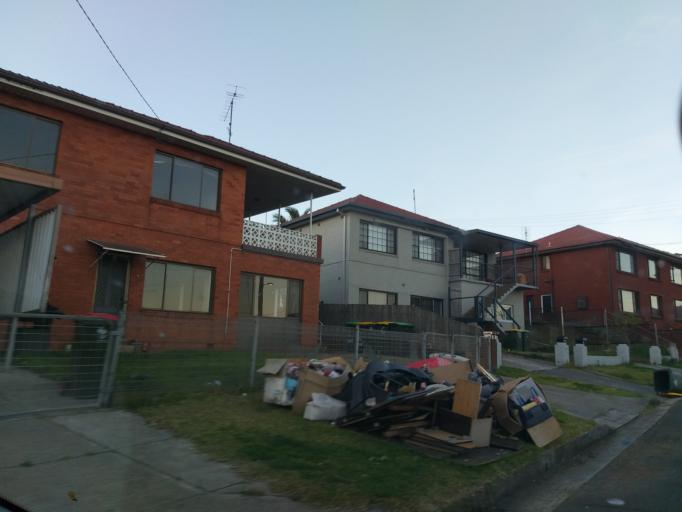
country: AU
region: New South Wales
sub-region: Wollongong
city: Lake Heights
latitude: -34.4808
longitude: 150.8862
